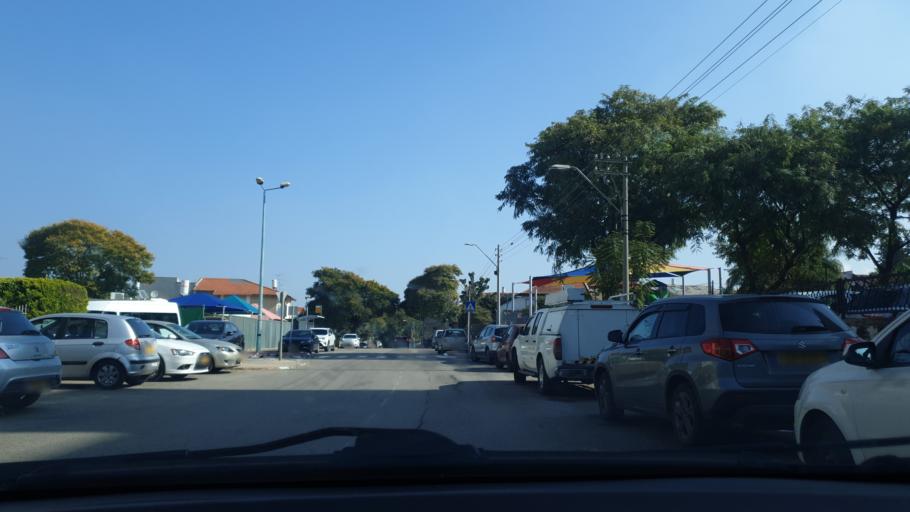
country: IL
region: Central District
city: Ramla
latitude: 31.9366
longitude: 34.8577
